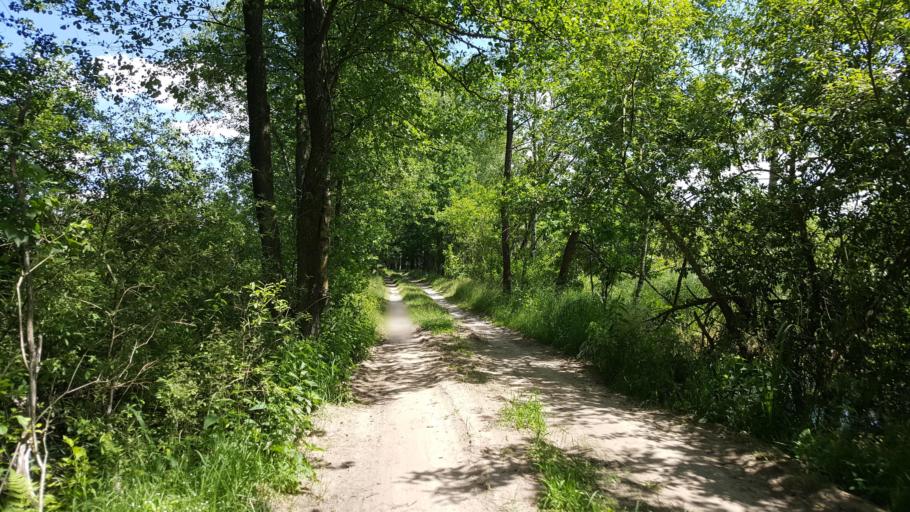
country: BY
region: Brest
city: Kamyanyuki
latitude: 52.5820
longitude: 23.7444
